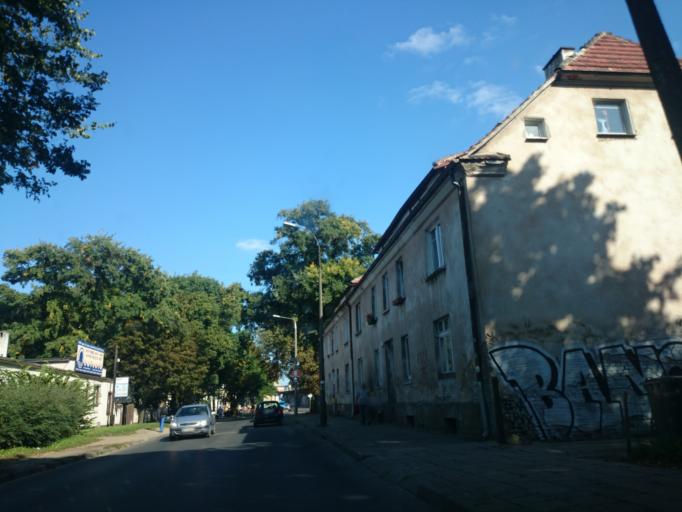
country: PL
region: Lubusz
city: Gorzow Wielkopolski
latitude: 52.7282
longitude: 15.2317
